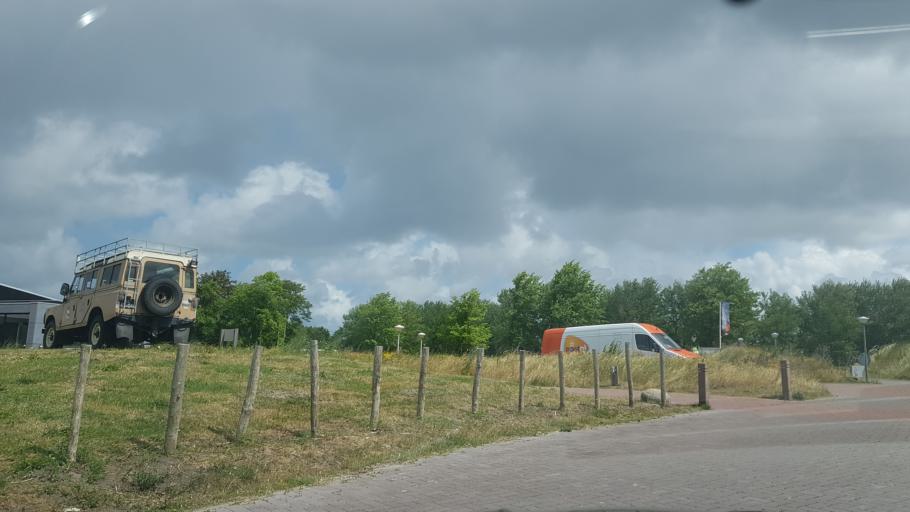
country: NL
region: Friesland
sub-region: Gemeente Dongeradeel
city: Anjum
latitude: 53.4032
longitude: 6.2116
